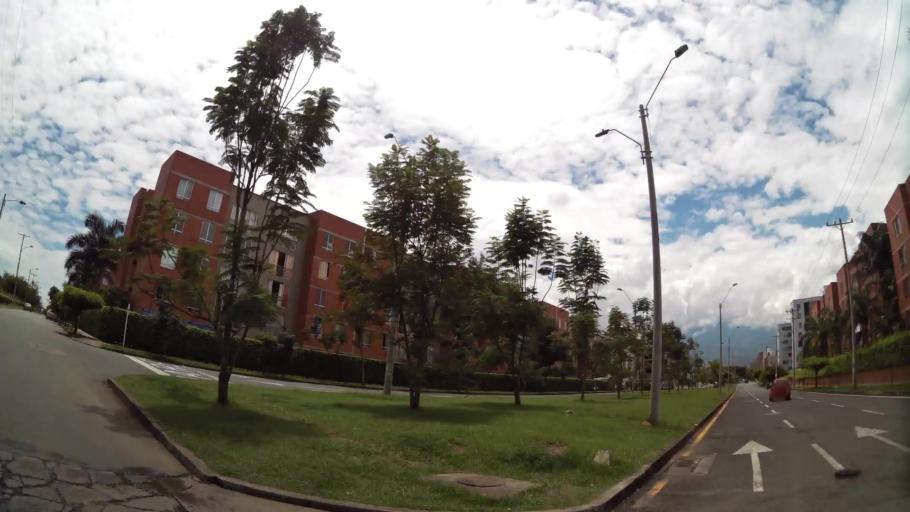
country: CO
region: Valle del Cauca
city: Cali
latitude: 3.3793
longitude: -76.5143
